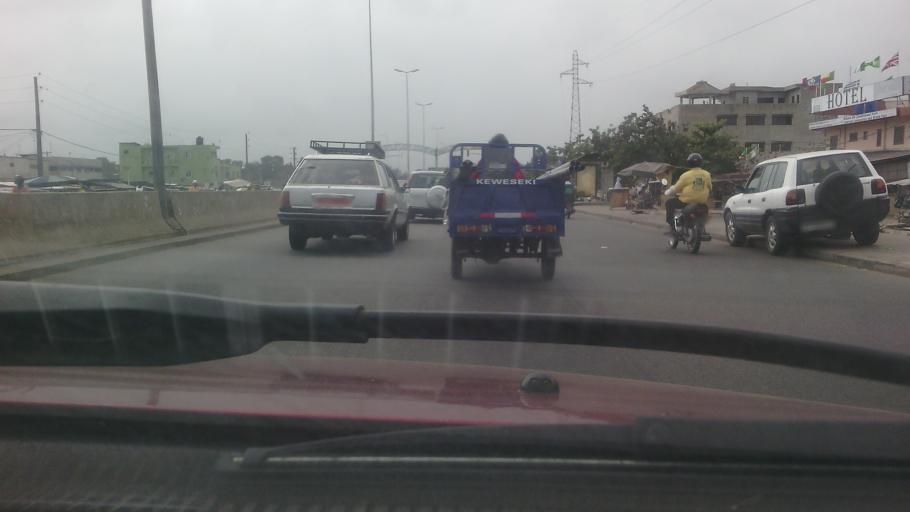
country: BJ
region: Littoral
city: Cotonou
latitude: 6.3697
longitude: 2.4934
